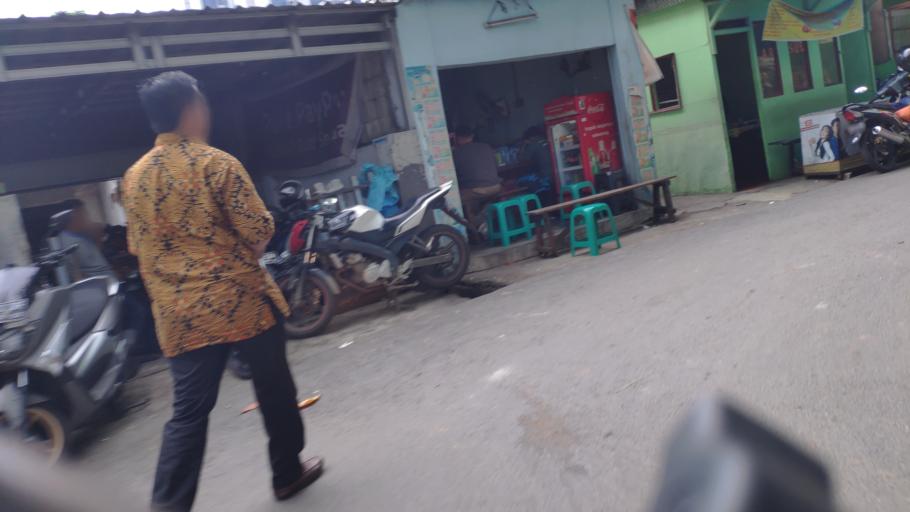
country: ID
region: Jakarta Raya
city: Jakarta
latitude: -6.2244
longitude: 106.8407
